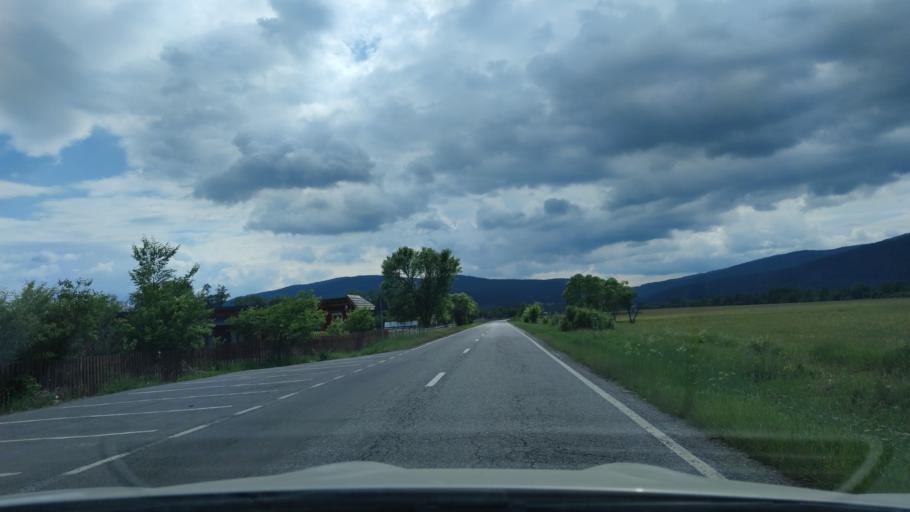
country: RO
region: Harghita
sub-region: Comuna Joseni
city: Joseni
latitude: 46.6827
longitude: 25.4066
